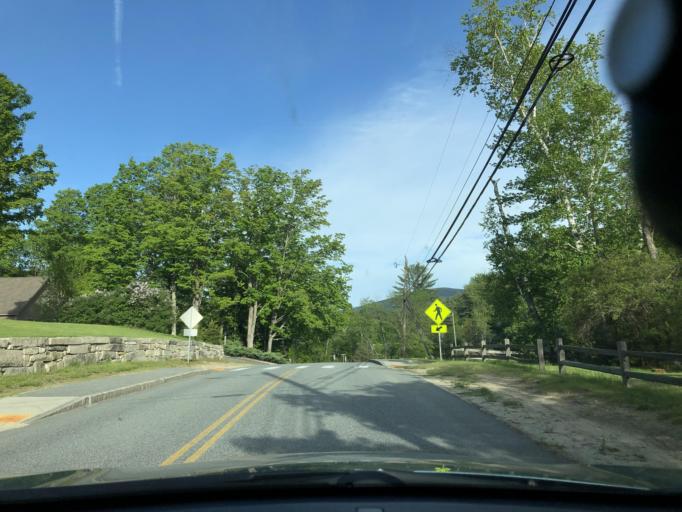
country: US
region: New Hampshire
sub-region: Merrimack County
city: Wilmot
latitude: 43.4191
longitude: -71.9352
